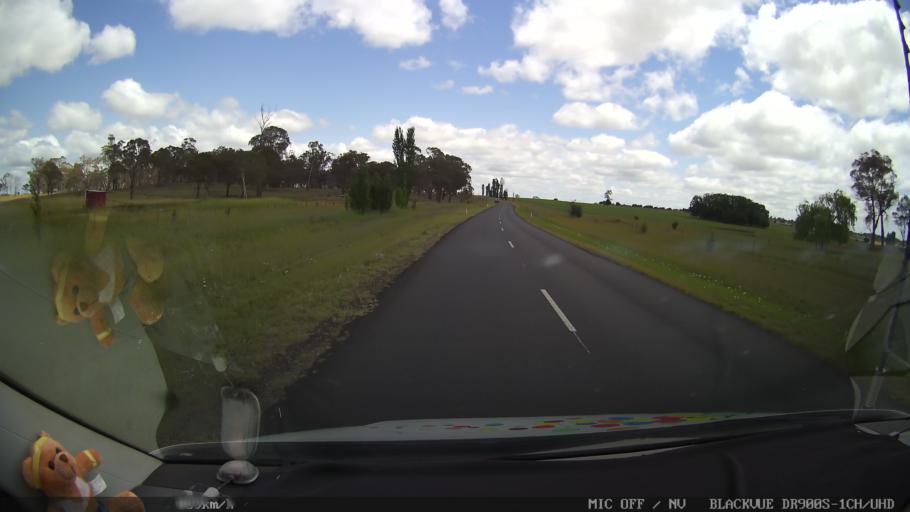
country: AU
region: New South Wales
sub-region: Glen Innes Severn
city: Glen Innes
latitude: -29.6673
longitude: 151.6942
